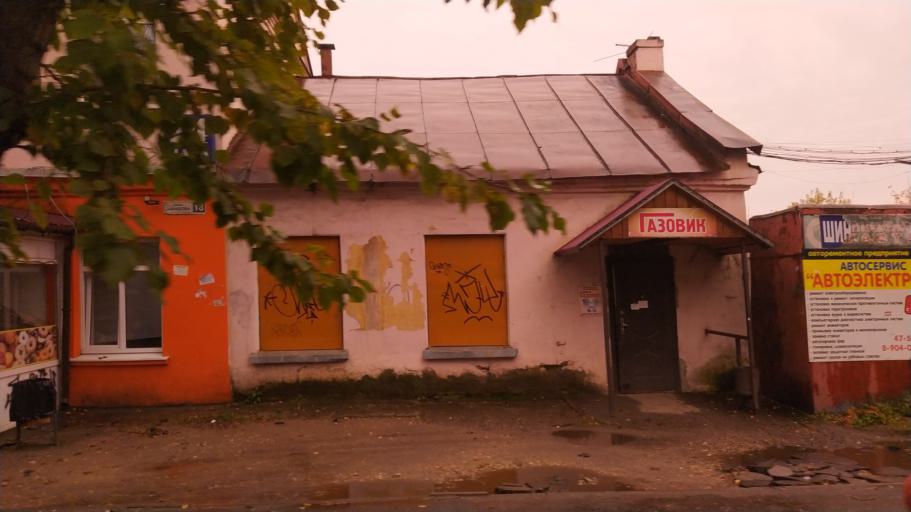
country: RU
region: Tverskaya
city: Tver
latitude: 56.8351
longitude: 35.9013
